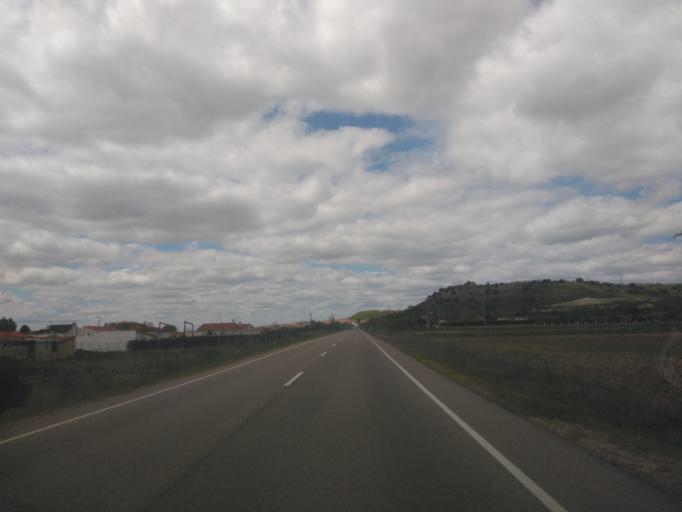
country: ES
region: Castille and Leon
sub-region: Provincia de Salamanca
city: Almenara de Tormes
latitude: 41.0577
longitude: -5.8044
